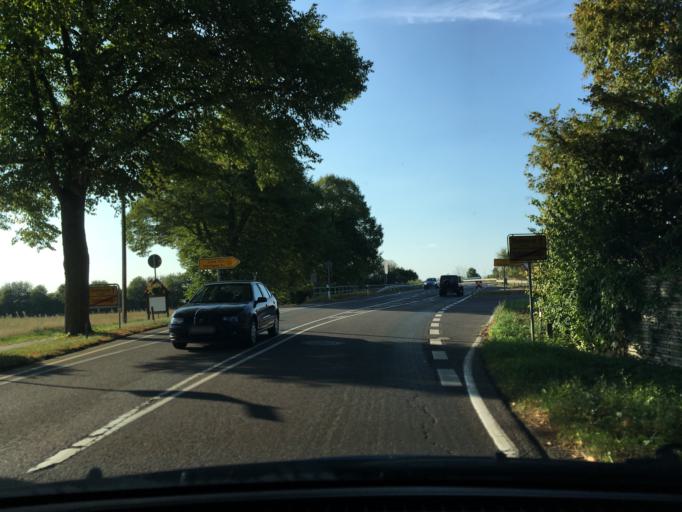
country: DE
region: Lower Saxony
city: Burgdorf
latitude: 52.4693
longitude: 9.9702
